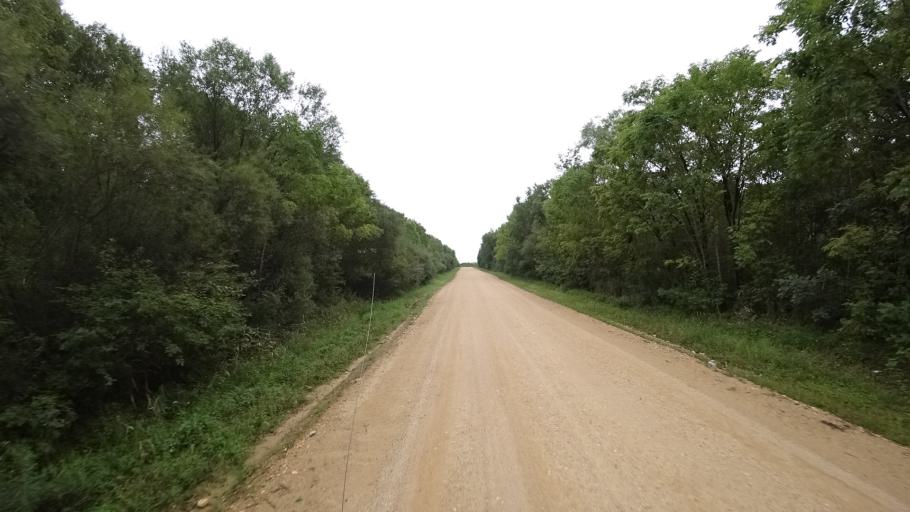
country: RU
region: Primorskiy
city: Monastyrishche
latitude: 44.0838
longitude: 132.5954
